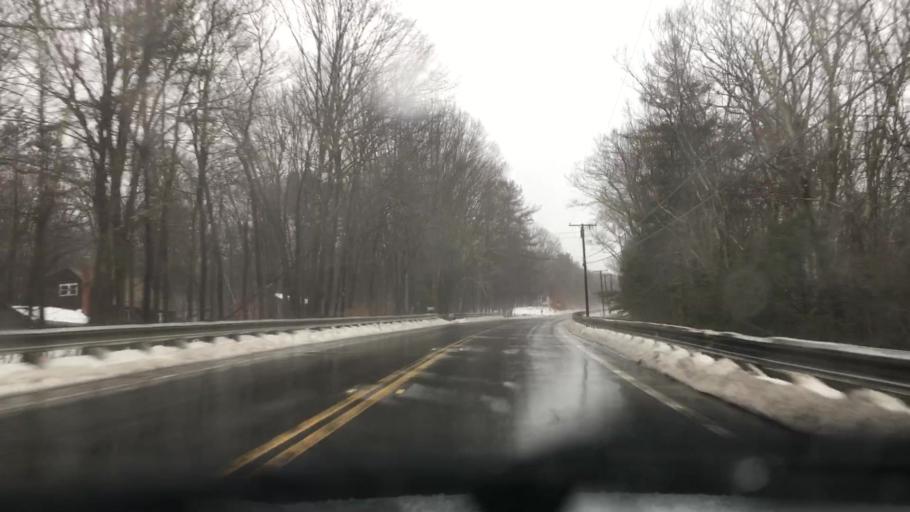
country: US
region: Massachusetts
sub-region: Hampshire County
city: Belchertown
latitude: 42.3225
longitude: -72.4059
